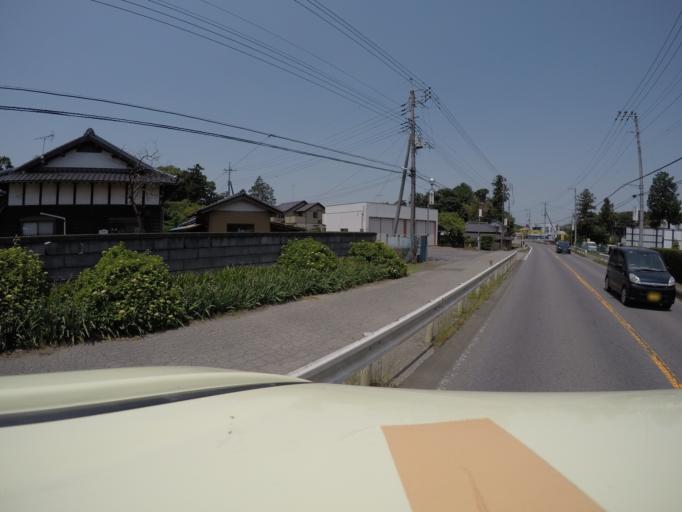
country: JP
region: Ibaraki
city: Iwai
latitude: 36.0380
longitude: 139.9360
